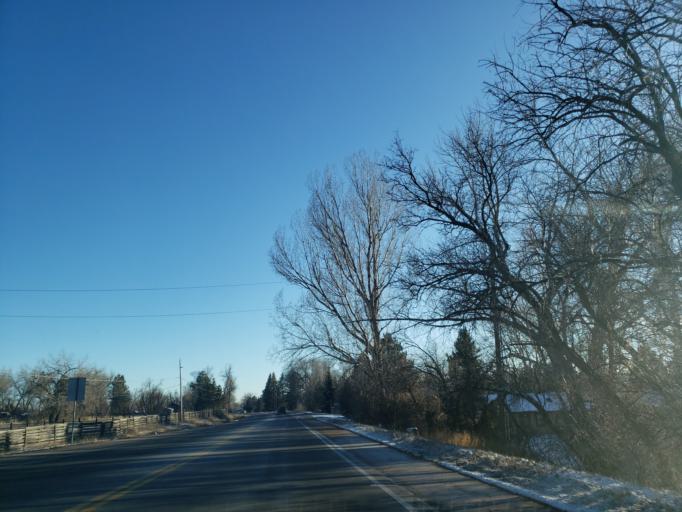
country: US
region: Colorado
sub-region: Larimer County
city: Fort Collins
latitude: 40.6307
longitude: -105.0713
